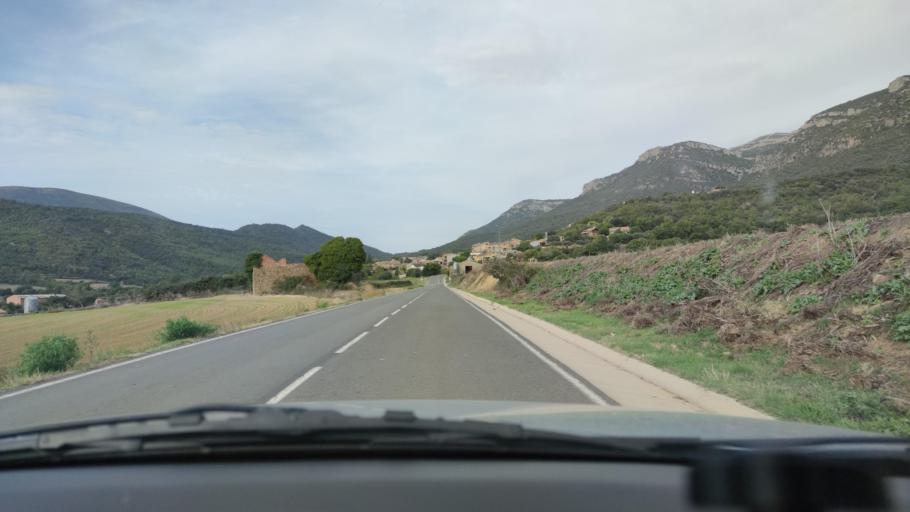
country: ES
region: Catalonia
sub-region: Provincia de Lleida
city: Artesa de Segre
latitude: 41.9914
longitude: 1.0011
